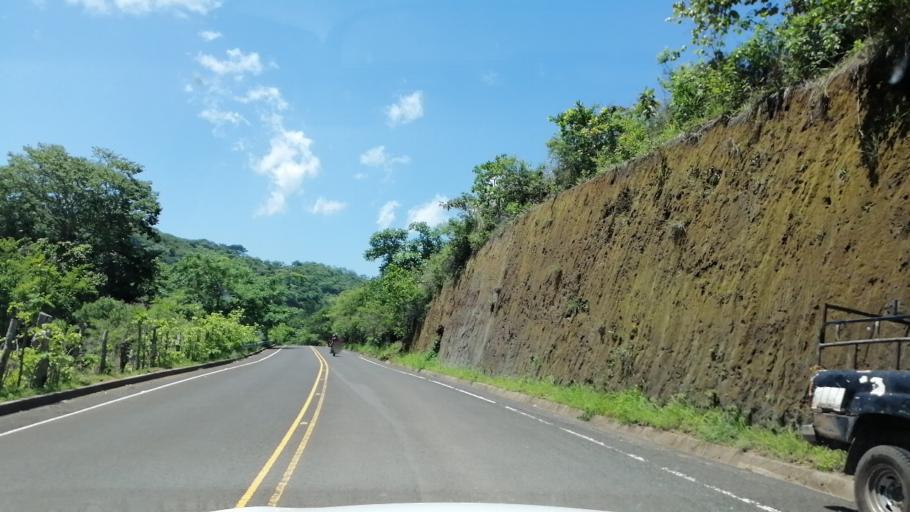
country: SV
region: San Miguel
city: Ciudad Barrios
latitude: 13.7974
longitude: -88.2954
